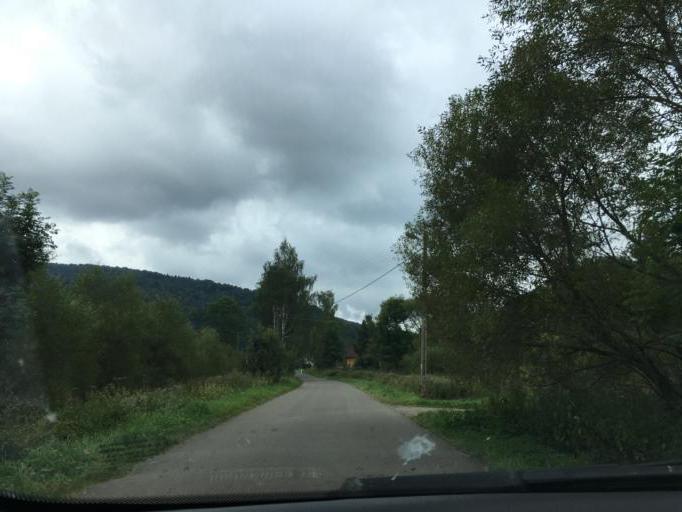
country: PL
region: Subcarpathian Voivodeship
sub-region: Powiat bieszczadzki
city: Lutowiska
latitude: 49.1792
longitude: 22.6028
